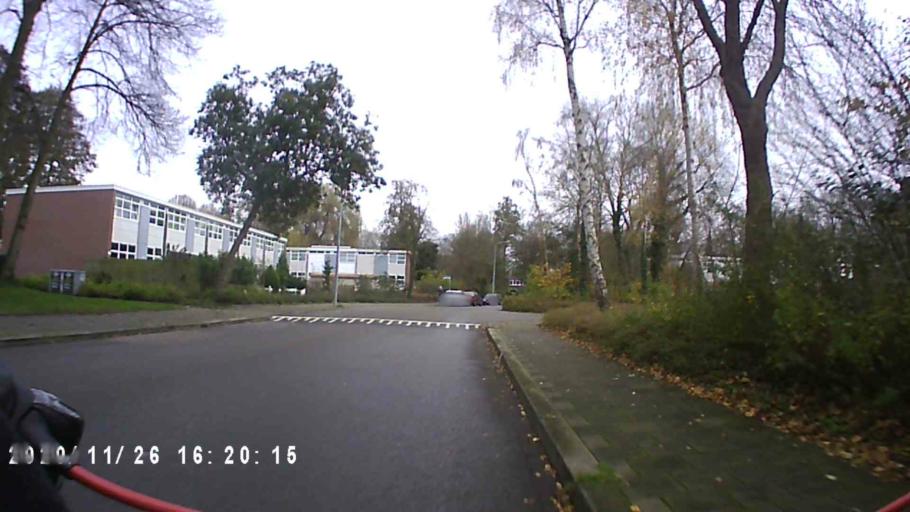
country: NL
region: Groningen
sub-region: Gemeente Groningen
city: Oosterpark
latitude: 53.2346
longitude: 6.6251
